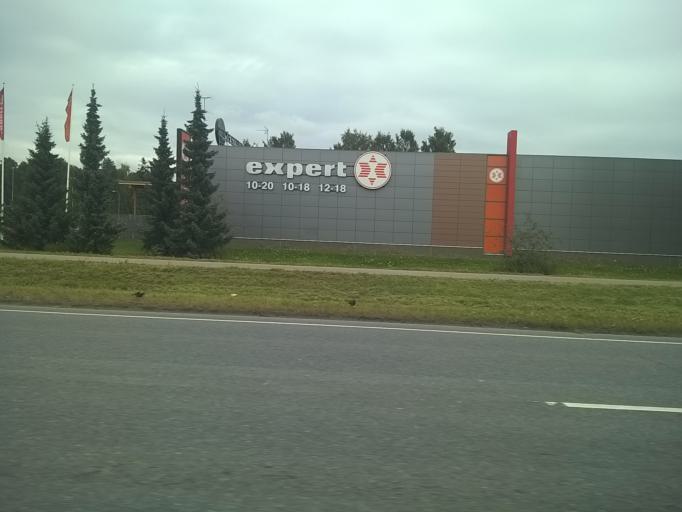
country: FI
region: Pirkanmaa
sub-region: Tampere
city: Tampere
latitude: 61.4925
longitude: 23.8224
